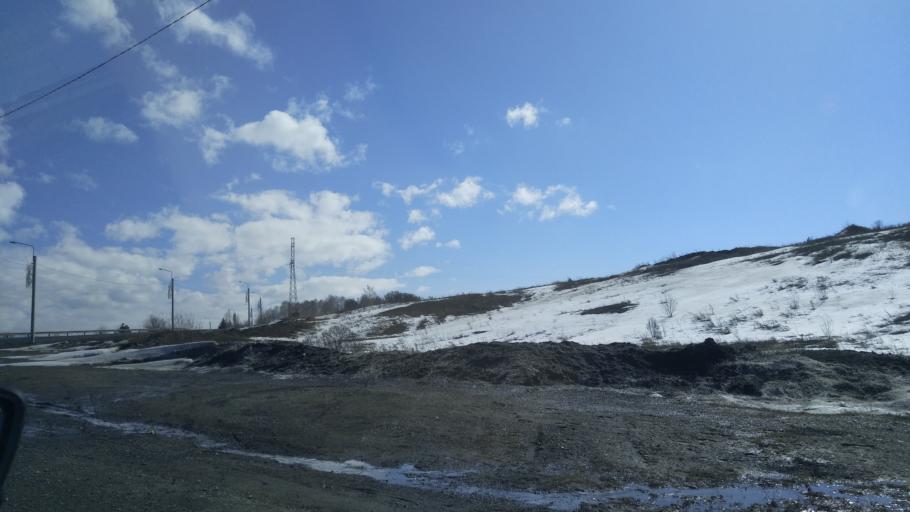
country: RU
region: Kemerovo
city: Yurga
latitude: 55.6990
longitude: 84.9589
